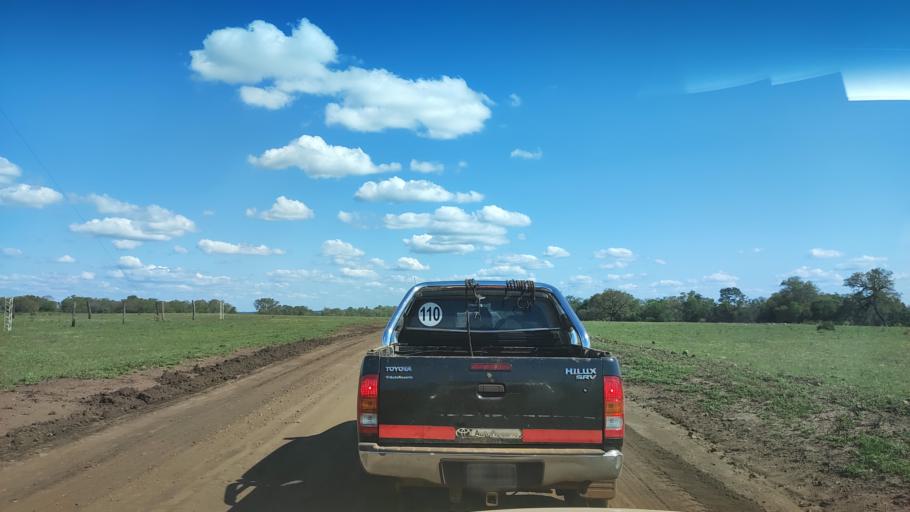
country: PY
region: Itapua
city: Carmen del Parana
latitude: -27.4153
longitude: -56.1719
